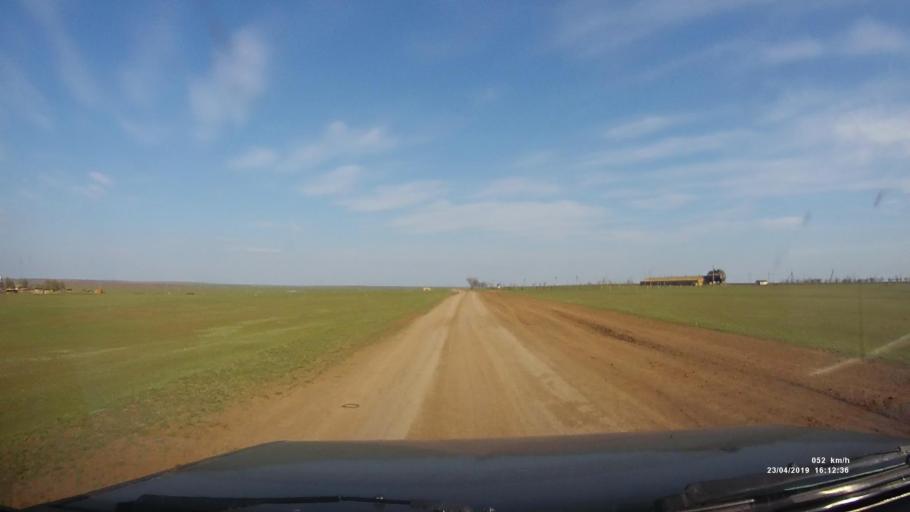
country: RU
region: Kalmykiya
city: Priyutnoye
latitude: 46.4660
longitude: 43.1294
